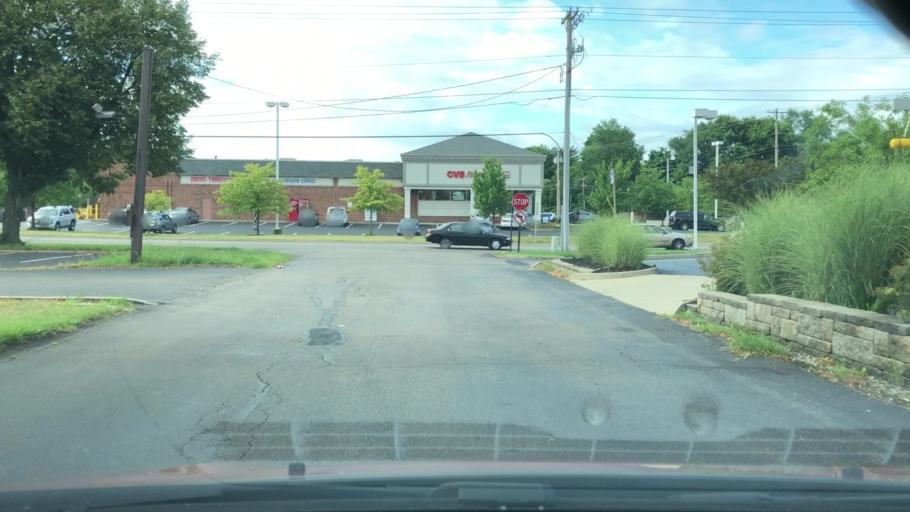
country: US
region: Ohio
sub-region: Montgomery County
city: Centerville
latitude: 39.6585
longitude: -84.1585
